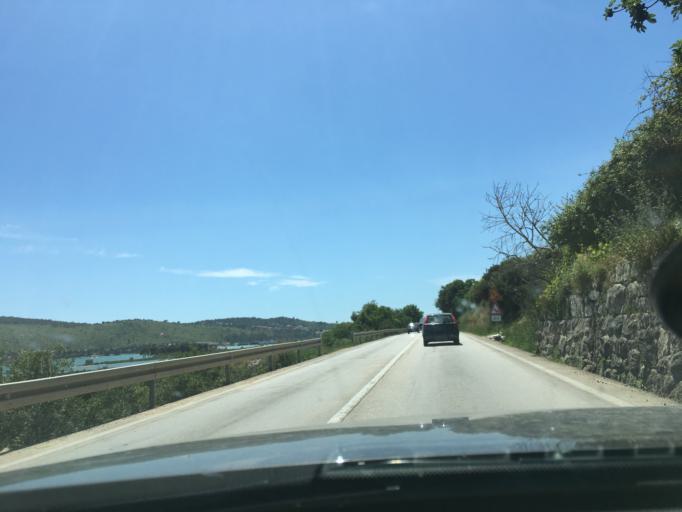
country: HR
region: Splitsko-Dalmatinska
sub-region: Grad Trogir
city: Trogir
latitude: 43.5286
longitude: 16.2742
